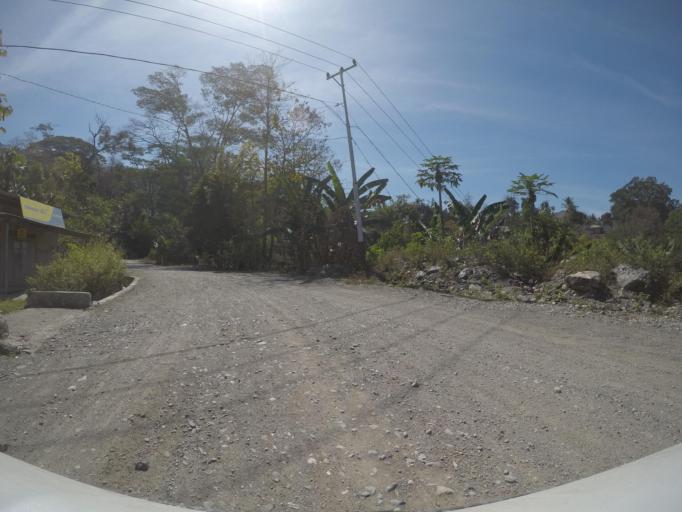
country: TL
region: Ermera
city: Gleno
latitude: -8.8092
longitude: 125.3172
